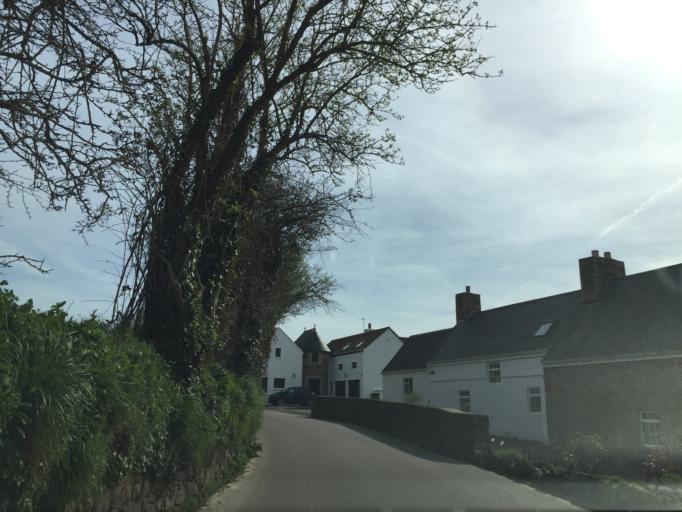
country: JE
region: St Helier
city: Saint Helier
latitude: 49.2330
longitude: -2.0990
